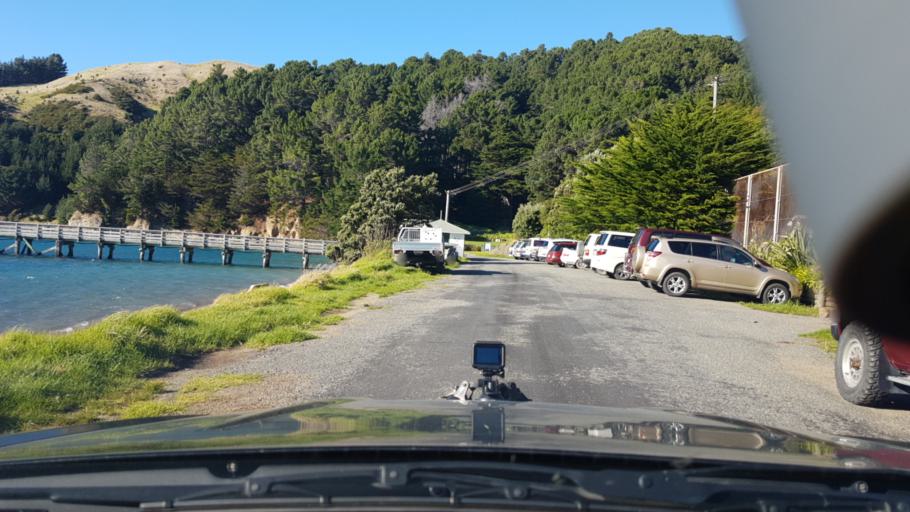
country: NZ
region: Marlborough
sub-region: Marlborough District
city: Picton
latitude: -40.9264
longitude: 173.8429
